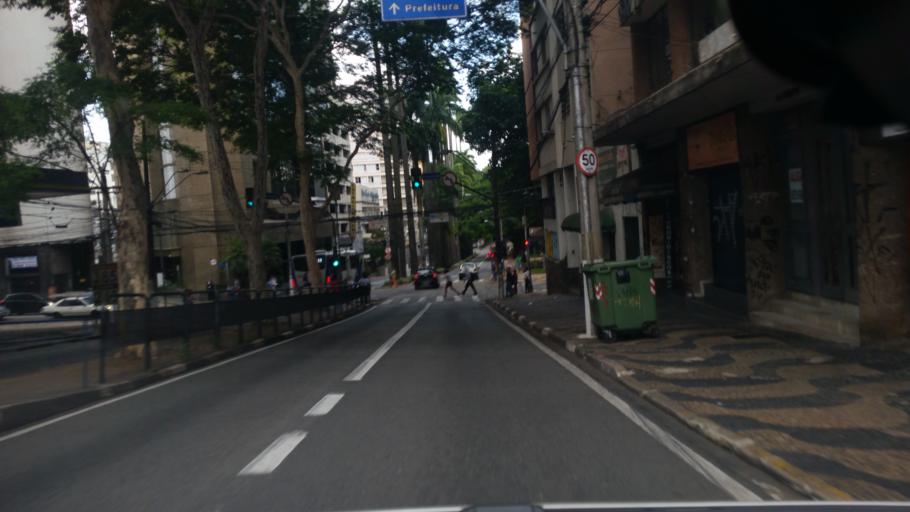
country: BR
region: Sao Paulo
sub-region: Campinas
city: Campinas
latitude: -22.9047
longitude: -47.0563
